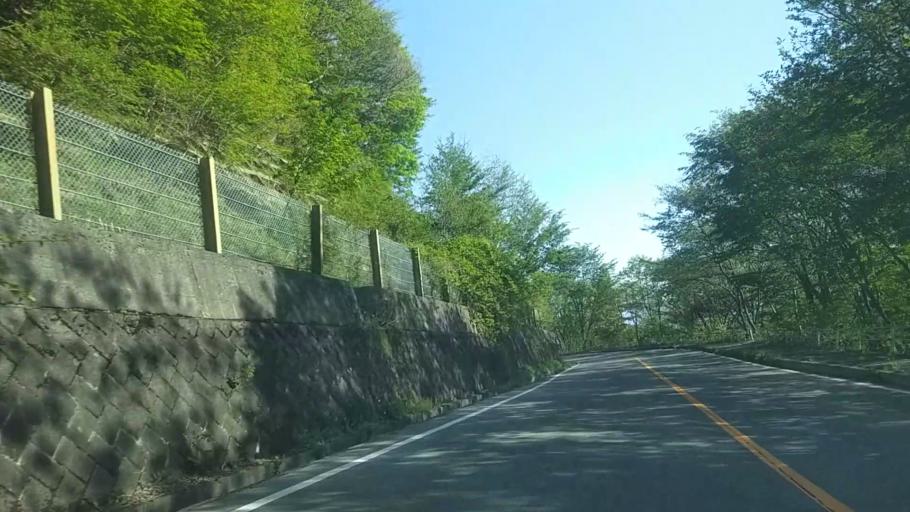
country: JP
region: Yamanashi
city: Nirasaki
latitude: 35.9053
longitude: 138.3819
